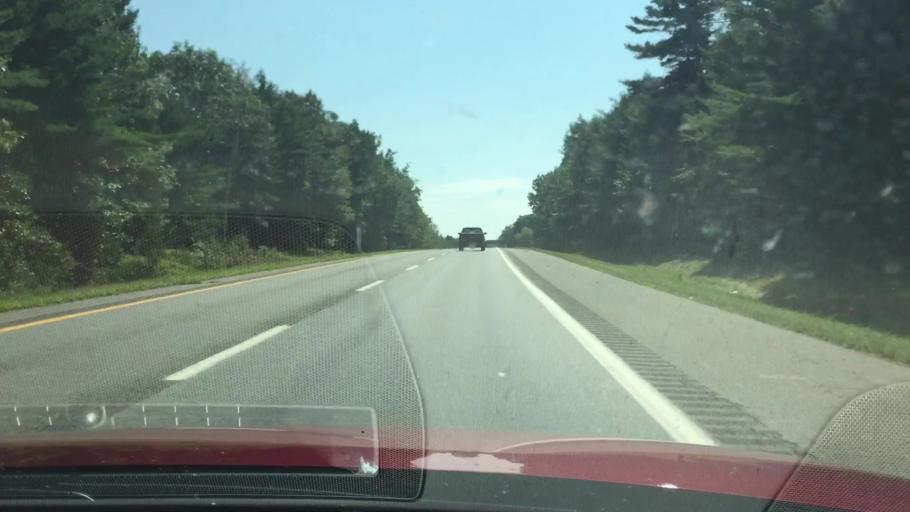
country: US
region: Maine
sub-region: Penobscot County
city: Orono
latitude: 44.8937
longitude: -68.6919
